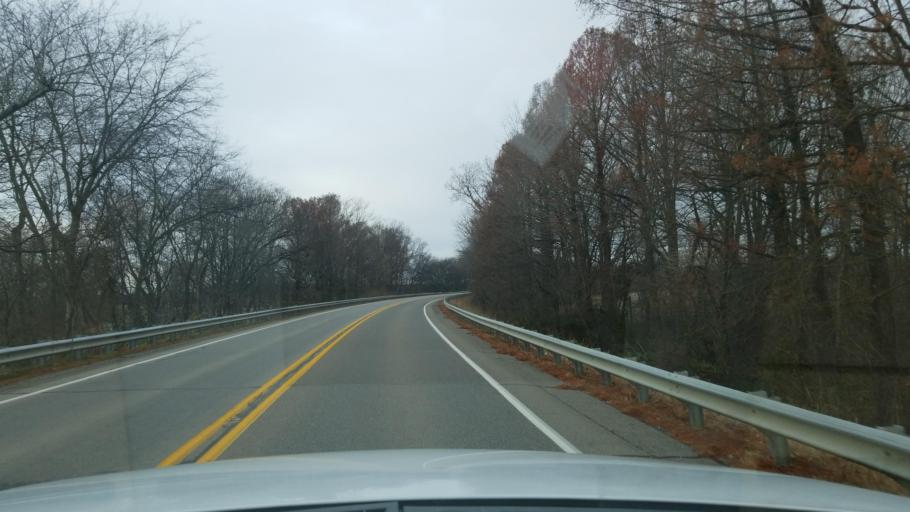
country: US
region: Indiana
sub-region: Posey County
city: Mount Vernon
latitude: 37.9292
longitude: -87.9979
